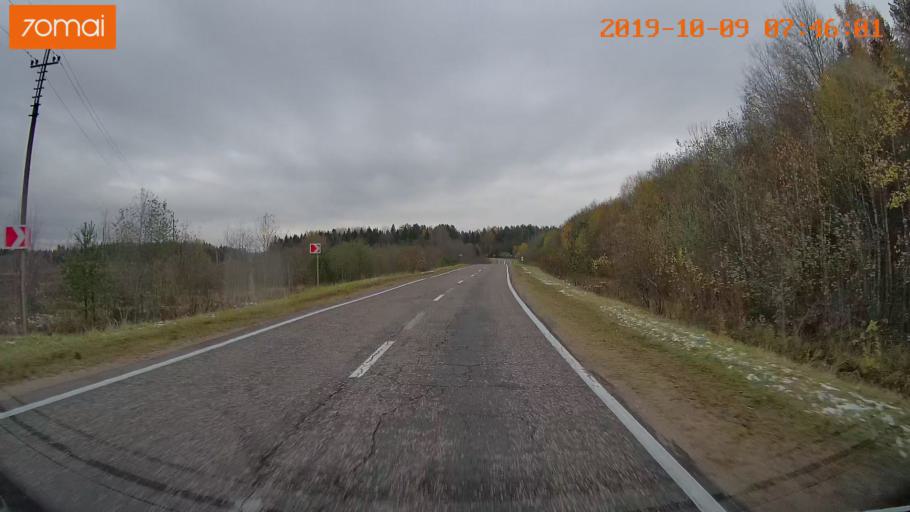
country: RU
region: Jaroslavl
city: Kukoboy
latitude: 58.6560
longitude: 39.7791
